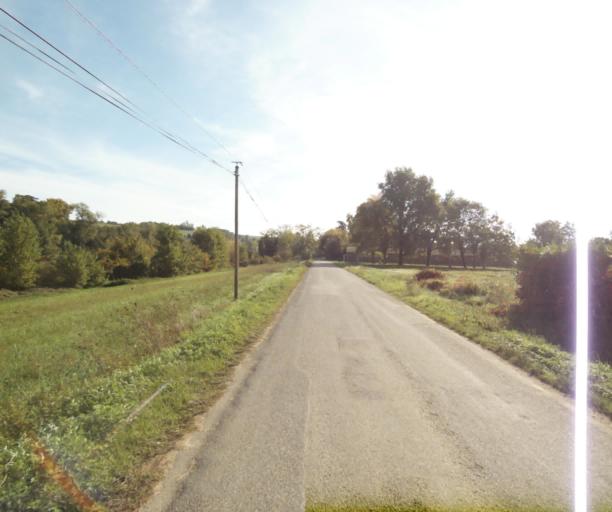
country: FR
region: Midi-Pyrenees
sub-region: Departement du Tarn-et-Garonne
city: Nohic
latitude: 43.9052
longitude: 1.4463
